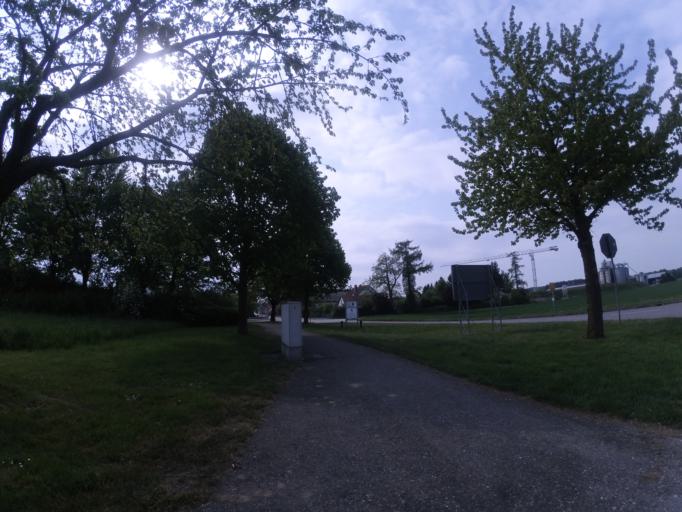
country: DE
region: Baden-Wuerttemberg
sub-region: Tuebingen Region
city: Staig
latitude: 48.3327
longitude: 9.9624
